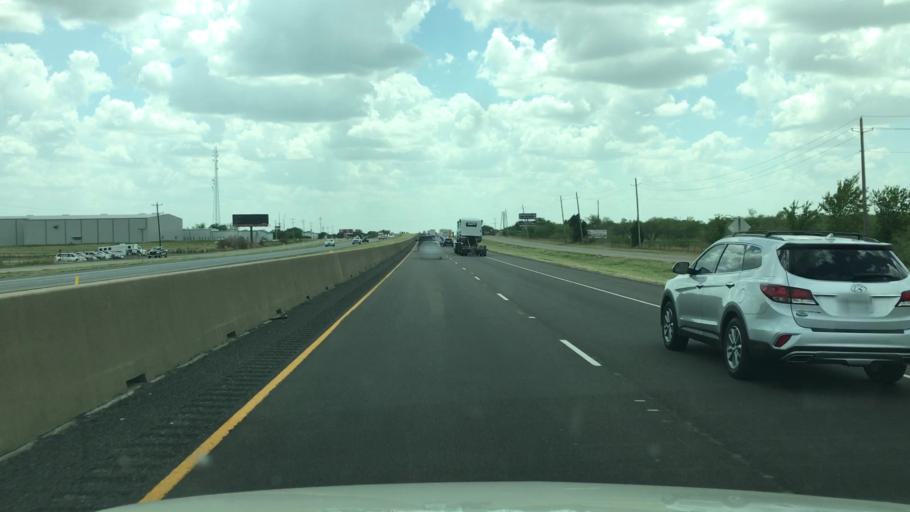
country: US
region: Texas
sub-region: Hunt County
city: Greenville
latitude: 33.0710
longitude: -96.1459
